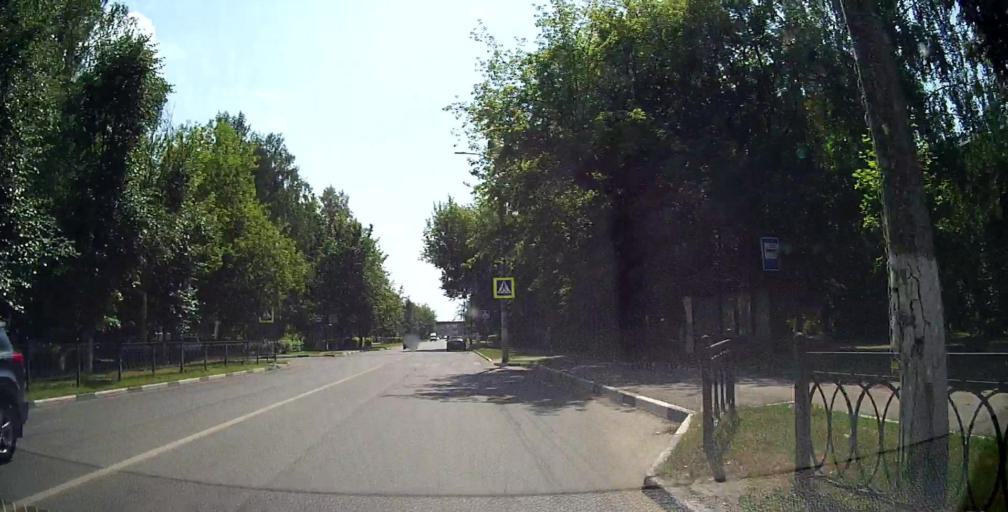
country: RU
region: Moskovskaya
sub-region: Podol'skiy Rayon
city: Podol'sk
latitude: 55.4173
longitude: 37.5319
